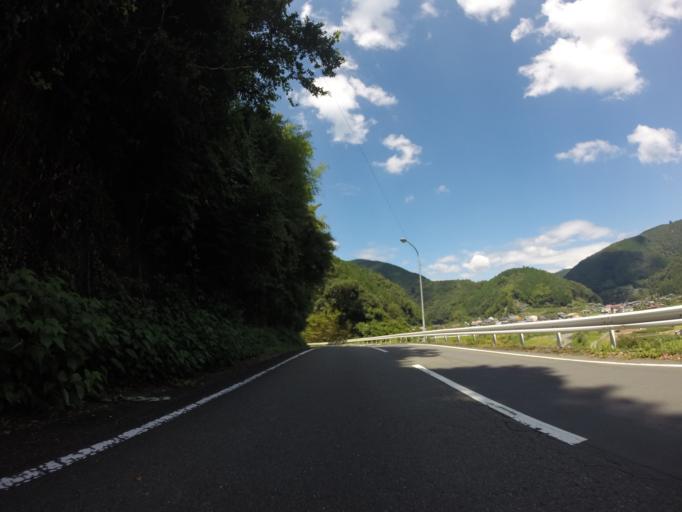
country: JP
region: Shizuoka
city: Shizuoka-shi
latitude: 35.0656
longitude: 138.2433
